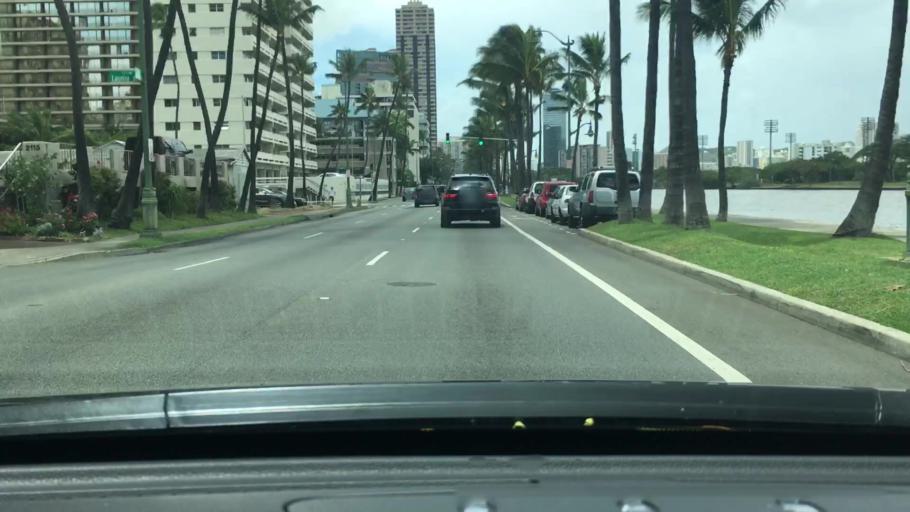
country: US
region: Hawaii
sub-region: Honolulu County
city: Honolulu
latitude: 21.2839
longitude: -157.8284
